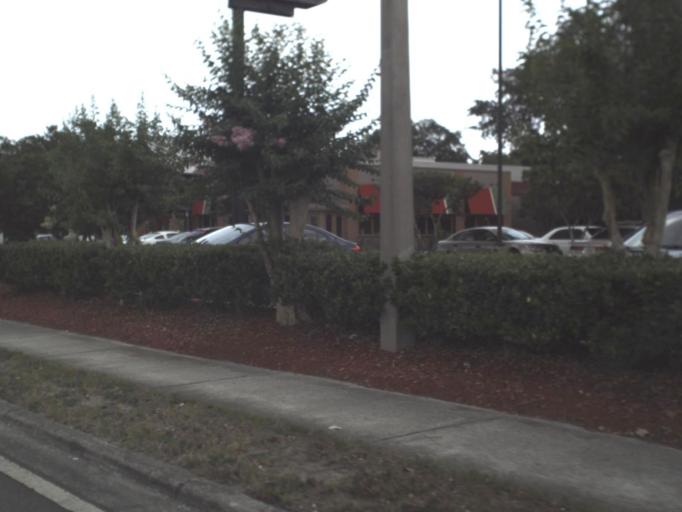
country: US
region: Florida
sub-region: Duval County
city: Jacksonville
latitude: 30.3173
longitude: -81.5573
